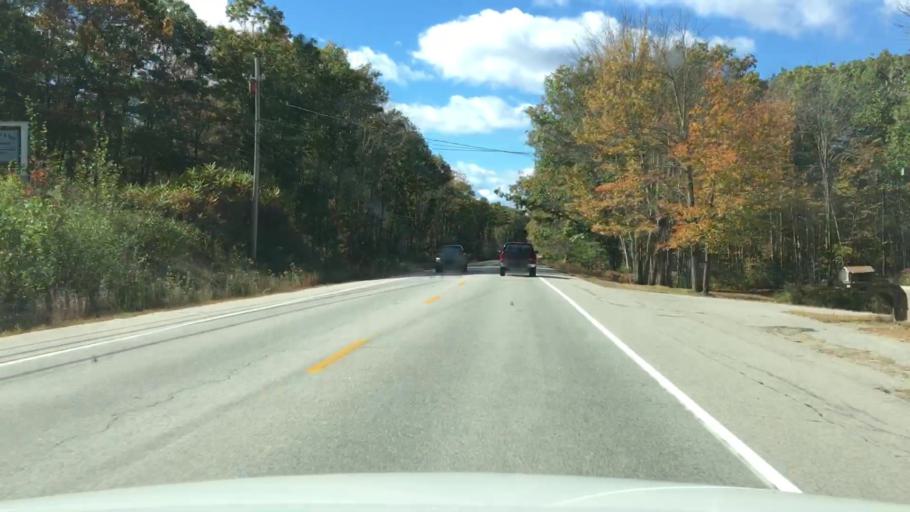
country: US
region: Maine
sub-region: York County
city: Alfred
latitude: 43.4762
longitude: -70.6661
